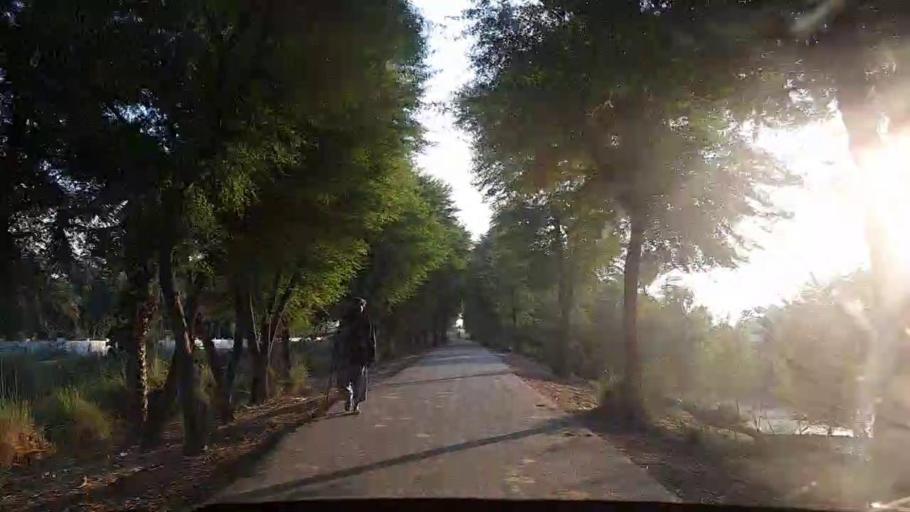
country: PK
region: Sindh
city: Sobhadero
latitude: 27.3901
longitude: 68.3839
